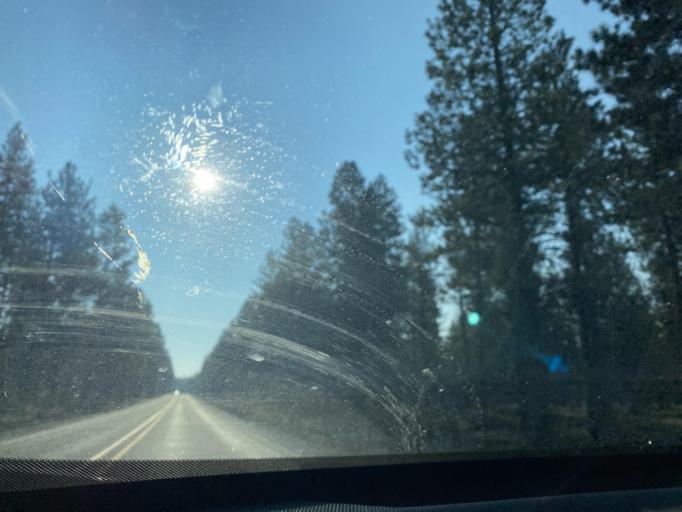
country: US
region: Oregon
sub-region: Deschutes County
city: Sunriver
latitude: 43.8694
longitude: -121.4234
